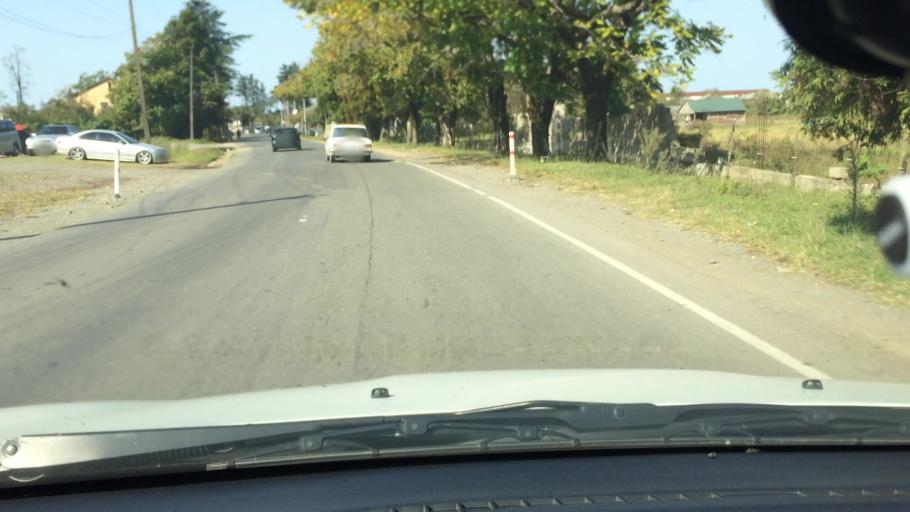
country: GE
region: Ajaria
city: Kobuleti
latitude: 41.8071
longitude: 41.7926
